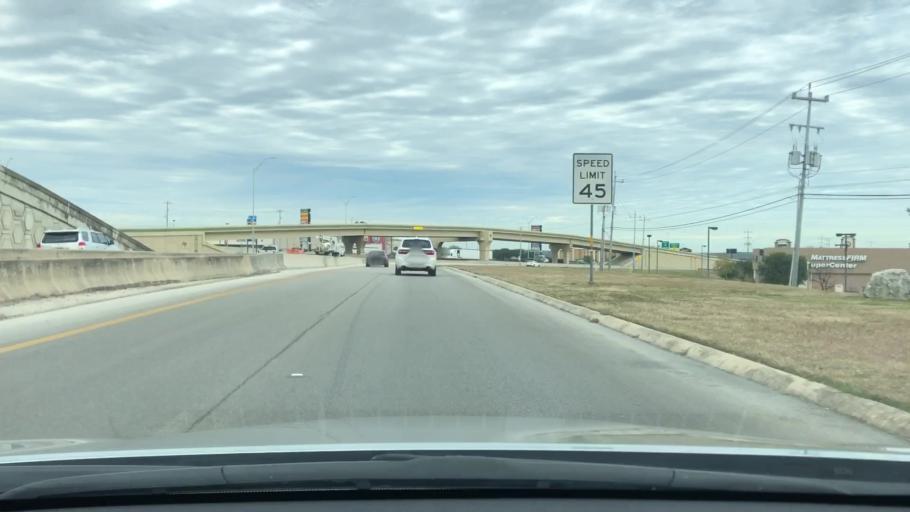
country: US
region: Texas
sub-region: Bexar County
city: Live Oak
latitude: 29.5678
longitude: -98.3311
